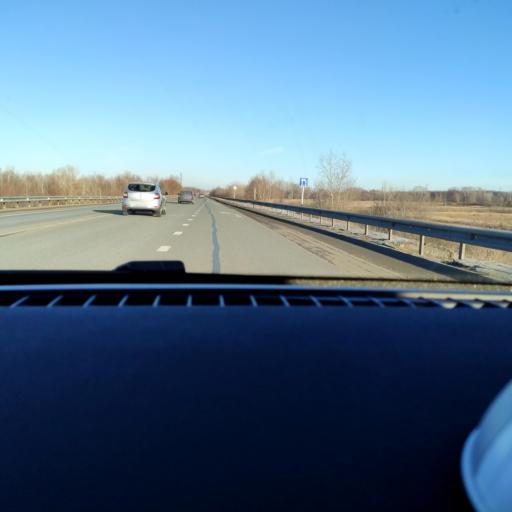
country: RU
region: Samara
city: Novokuybyshevsk
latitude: 53.1307
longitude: 49.9579
